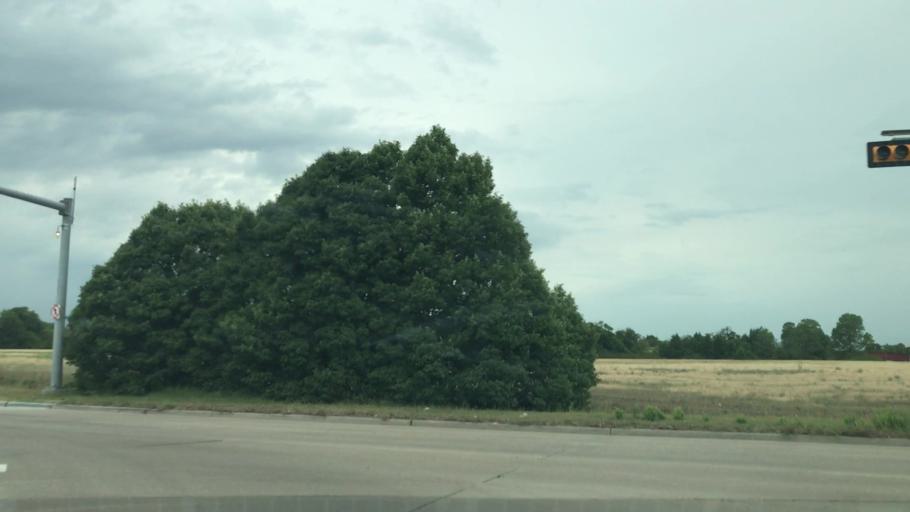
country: US
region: Texas
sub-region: Collin County
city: Plano
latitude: 33.0011
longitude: -96.7479
